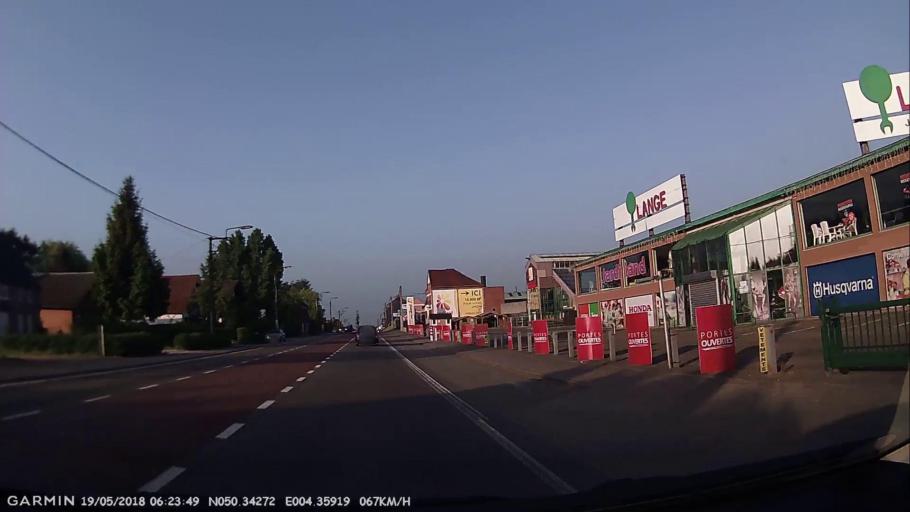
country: BE
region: Wallonia
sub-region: Province du Hainaut
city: Thuin
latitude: 50.3427
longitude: 4.3592
